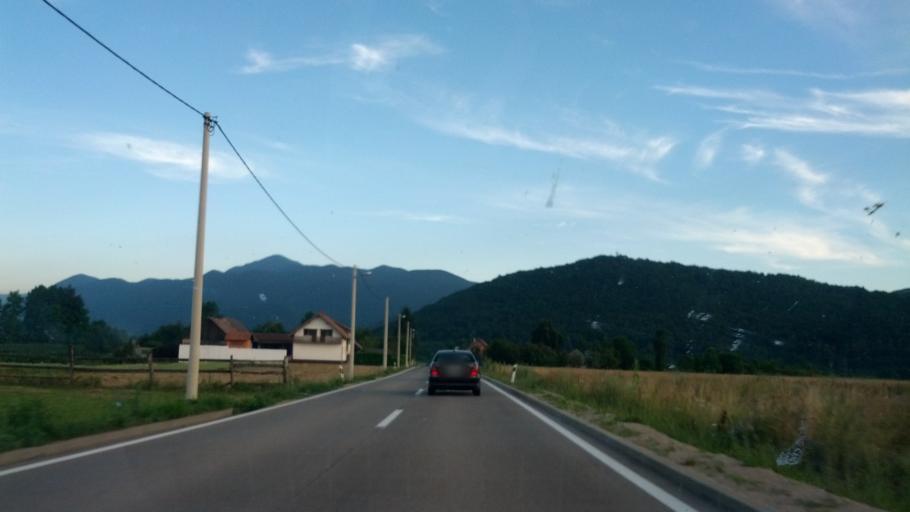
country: BA
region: Federation of Bosnia and Herzegovina
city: Izacic
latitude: 44.9006
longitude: 15.7242
